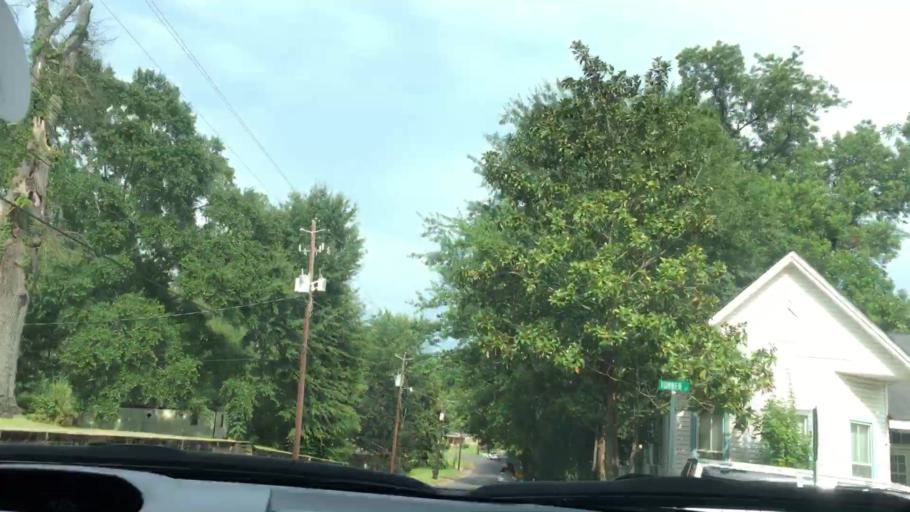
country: US
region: Alabama
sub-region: Hale County
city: Greensboro
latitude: 32.7055
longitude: -87.5913
